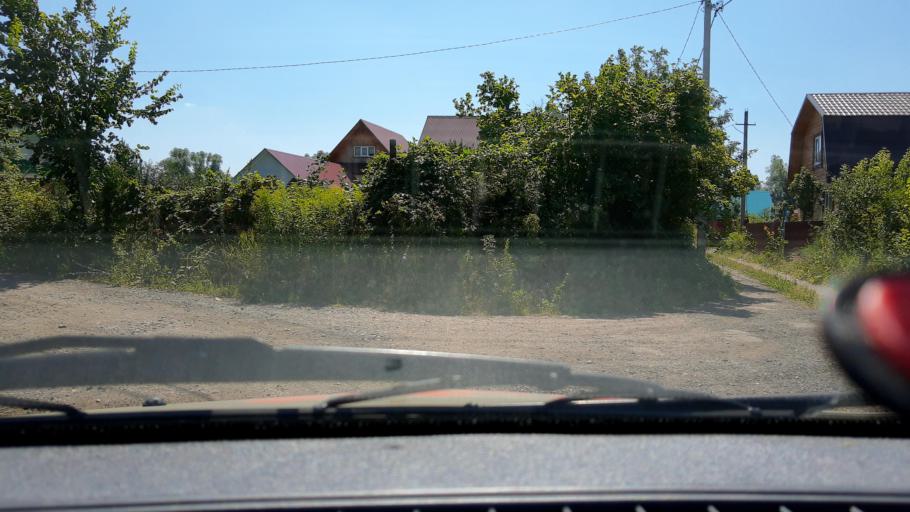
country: RU
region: Bashkortostan
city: Mikhaylovka
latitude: 54.7957
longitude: 55.8369
